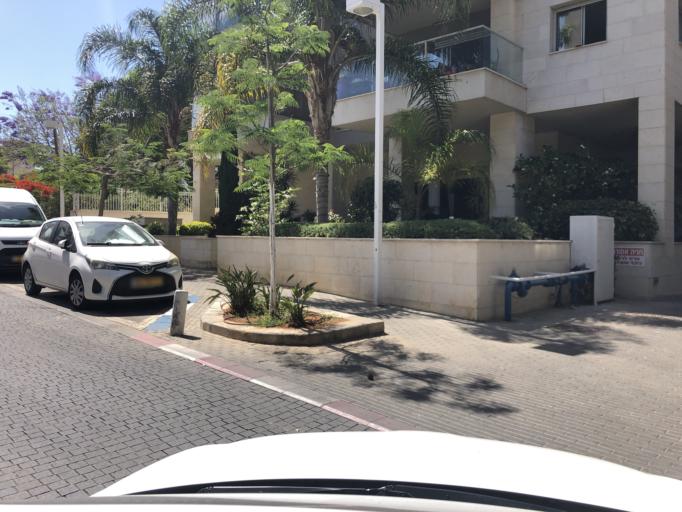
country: IL
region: Tel Aviv
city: Ramat Gan
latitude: 32.0779
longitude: 34.8122
